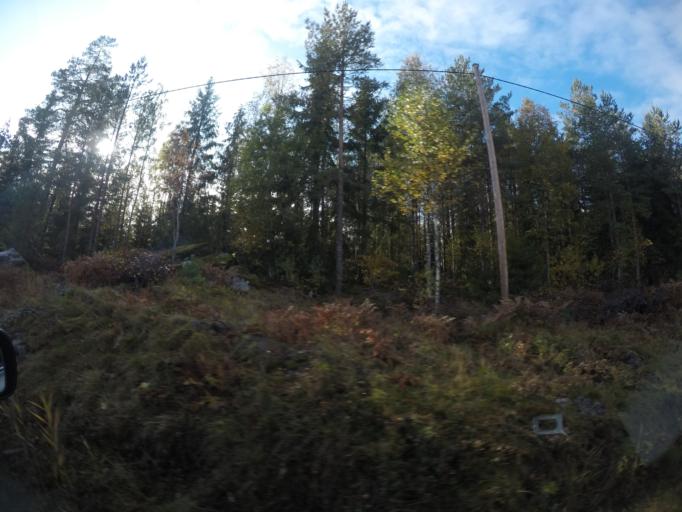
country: SE
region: Soedermanland
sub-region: Eskilstuna Kommun
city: Kvicksund
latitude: 59.3684
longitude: 16.2643
